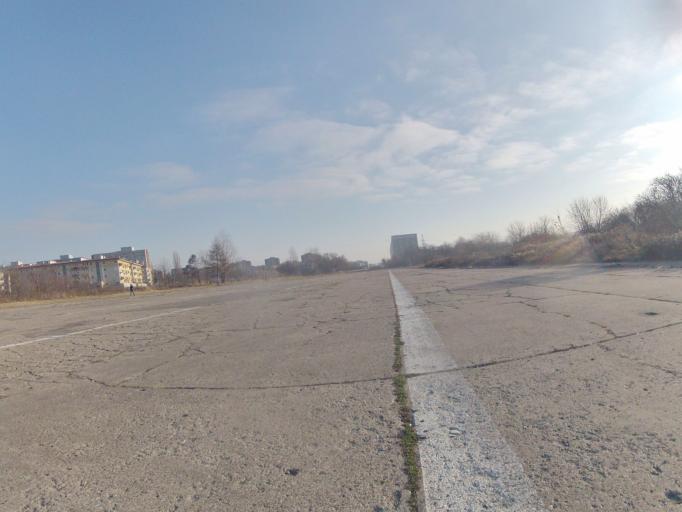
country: PL
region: Lesser Poland Voivodeship
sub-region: Krakow
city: Krakow
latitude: 50.0840
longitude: 19.9916
